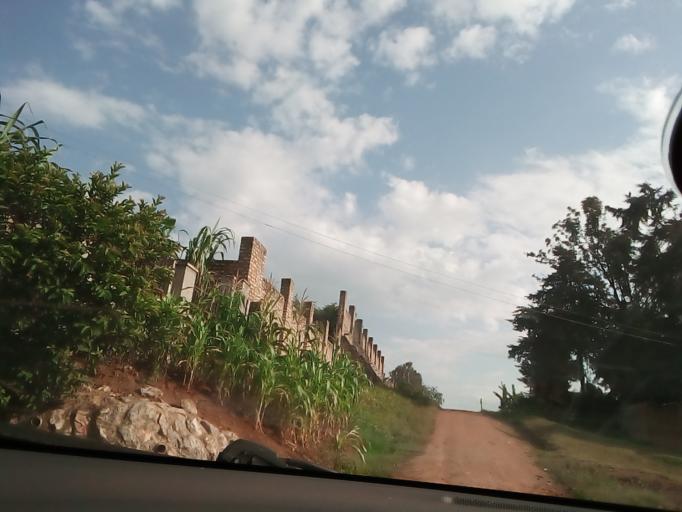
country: UG
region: Central Region
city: Masaka
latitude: -0.3522
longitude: 31.7444
